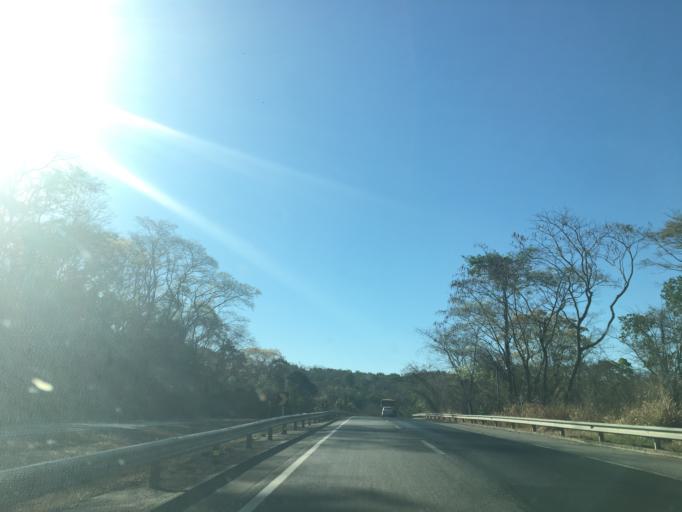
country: BR
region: Goias
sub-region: Hidrolandia
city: Hidrolandia
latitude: -17.0852
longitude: -49.2232
